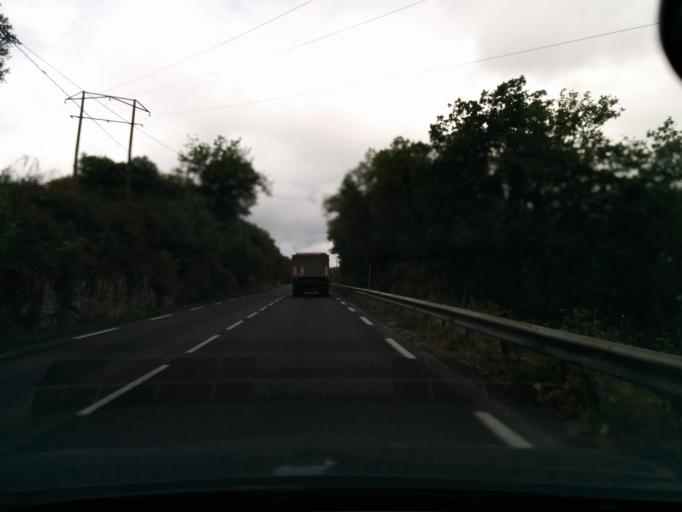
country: FR
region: Midi-Pyrenees
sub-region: Departement du Lot
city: Souillac
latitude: 44.9114
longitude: 1.4887
